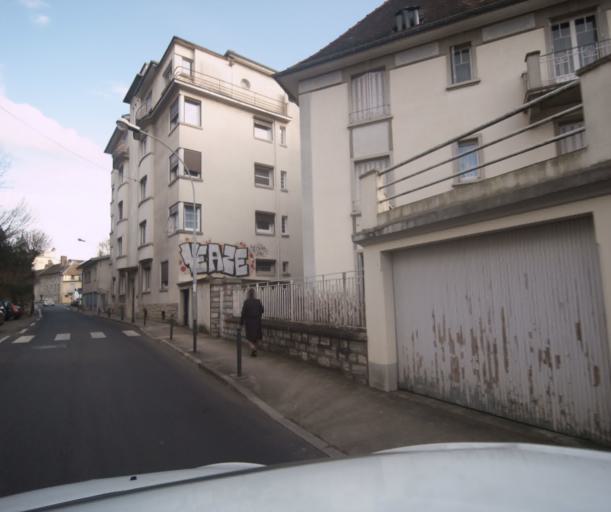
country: FR
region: Franche-Comte
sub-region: Departement du Doubs
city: Besancon
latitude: 47.2473
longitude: 6.0303
